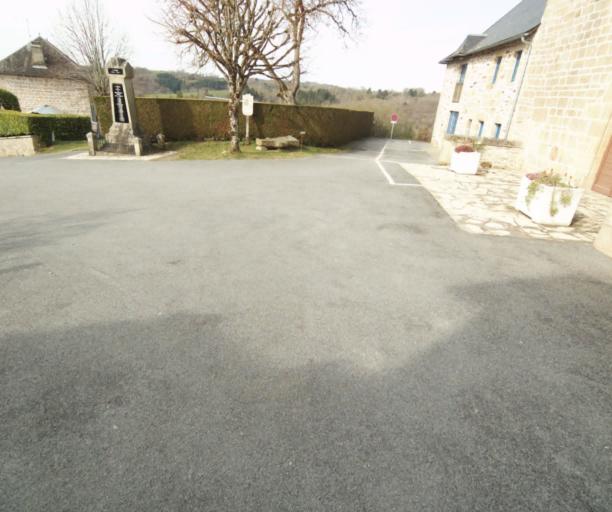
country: FR
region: Limousin
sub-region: Departement de la Correze
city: Correze
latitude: 45.4223
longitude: 1.8024
